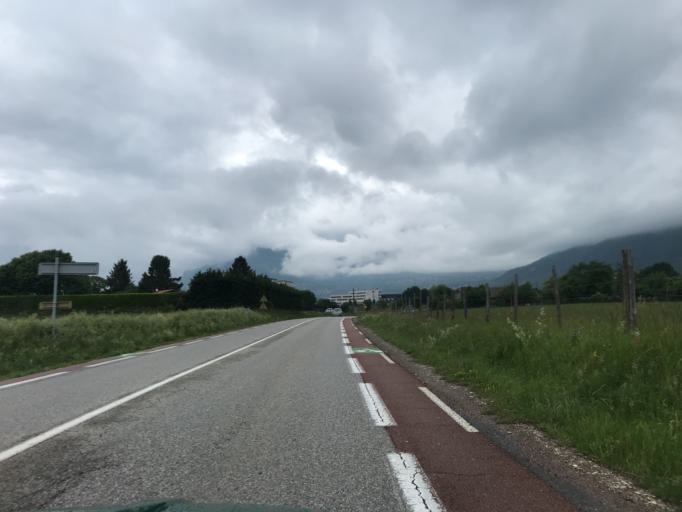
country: FR
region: Rhone-Alpes
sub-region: Departement de la Savoie
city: Saint-Baldoph
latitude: 45.5393
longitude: 5.9683
